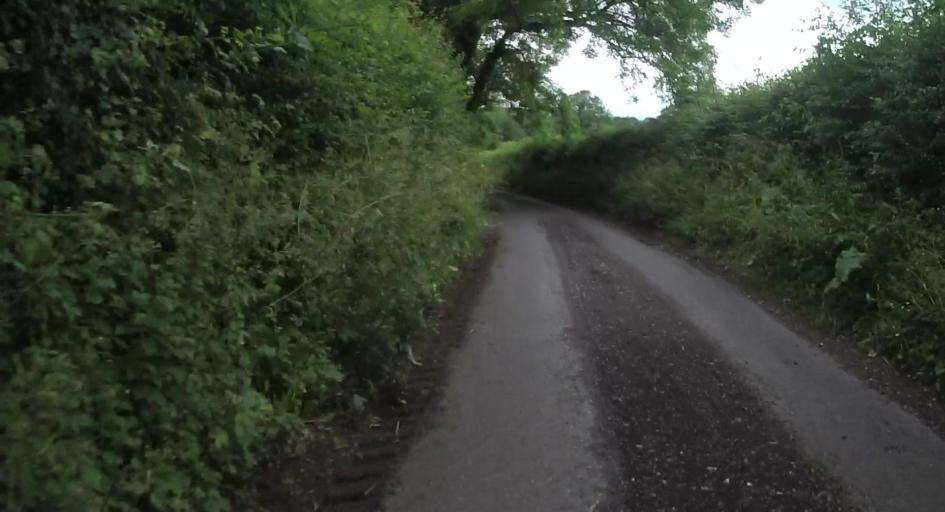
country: GB
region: England
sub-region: Hampshire
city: Kingsclere
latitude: 51.3164
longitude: -1.2208
